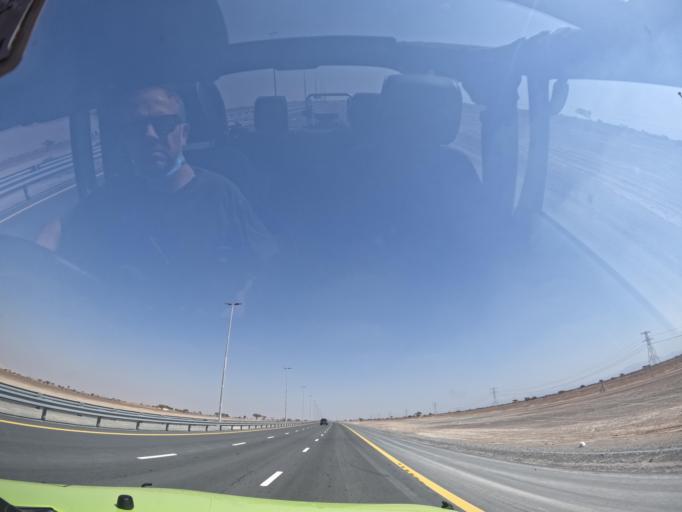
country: AE
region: Ash Shariqah
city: Adh Dhayd
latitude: 24.9430
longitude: 55.8288
